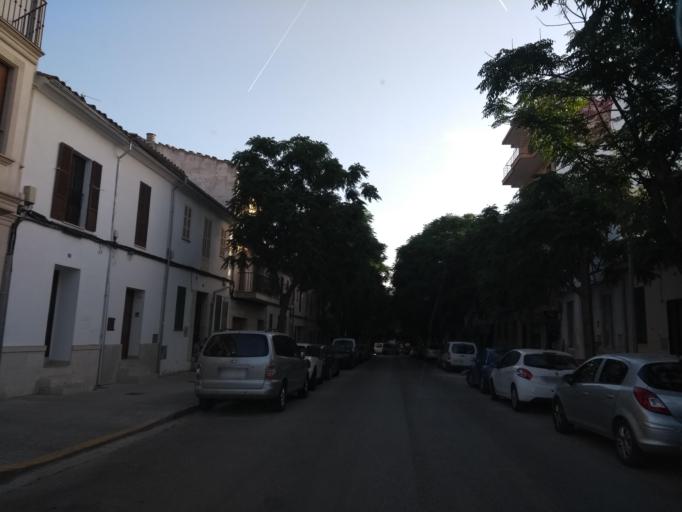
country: ES
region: Balearic Islands
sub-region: Illes Balears
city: Inca
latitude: 39.7243
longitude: 2.9174
